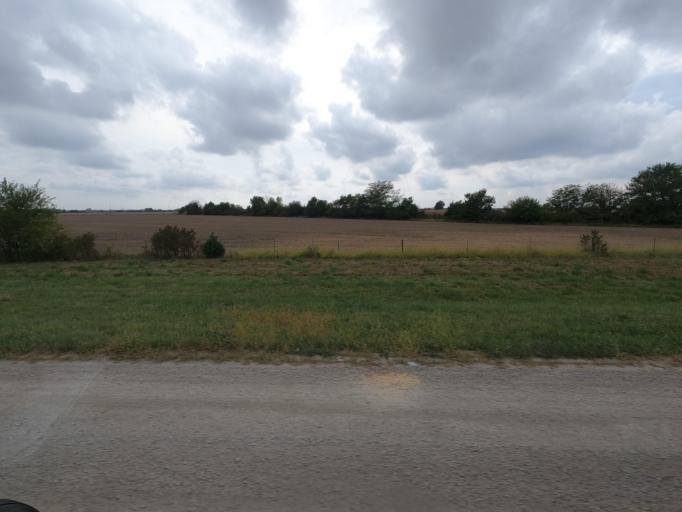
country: US
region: Iowa
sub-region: Wapello County
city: Ottumwa
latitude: 40.9984
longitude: -92.2405
